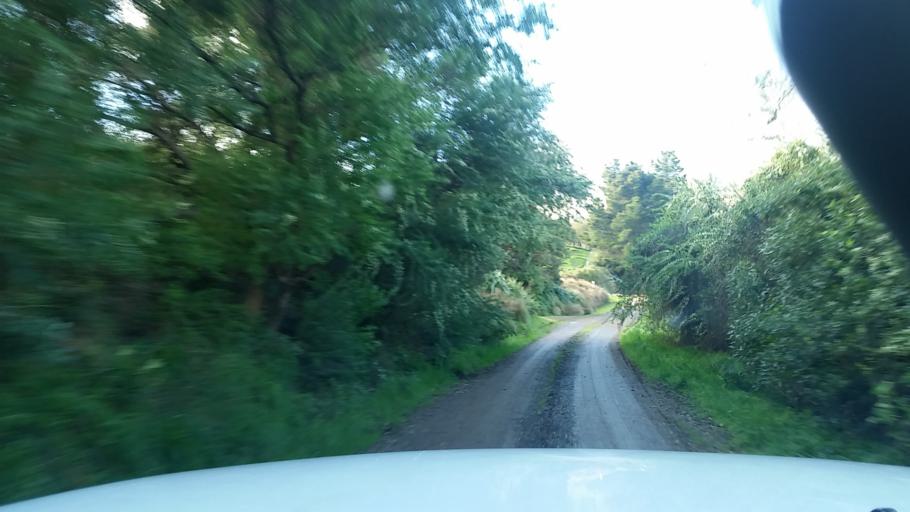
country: NZ
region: Canterbury
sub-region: Christchurch City
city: Christchurch
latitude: -43.7986
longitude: 172.9665
